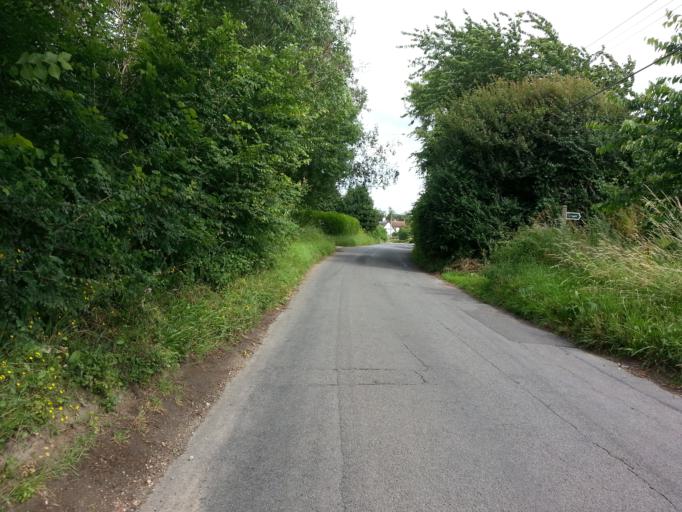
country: GB
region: England
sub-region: Suffolk
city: Ipswich
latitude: 51.9712
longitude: 1.1696
